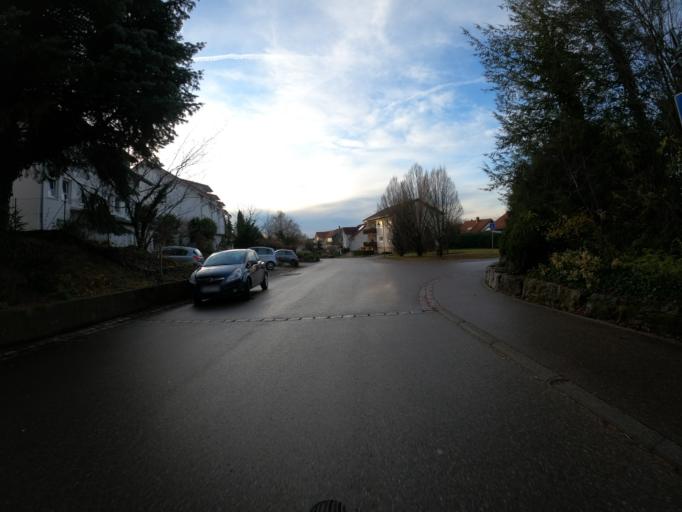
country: DE
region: Baden-Wuerttemberg
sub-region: Regierungsbezirk Stuttgart
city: Zell unter Aichelberg
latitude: 48.6479
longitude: 9.5770
